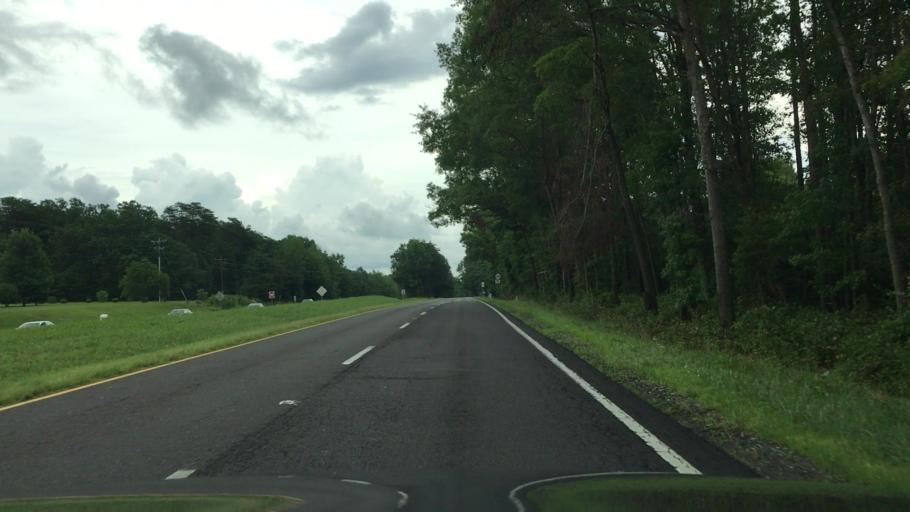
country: US
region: Virginia
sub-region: Spotsylvania County
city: Spotsylvania
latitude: 38.3206
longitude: -77.6987
